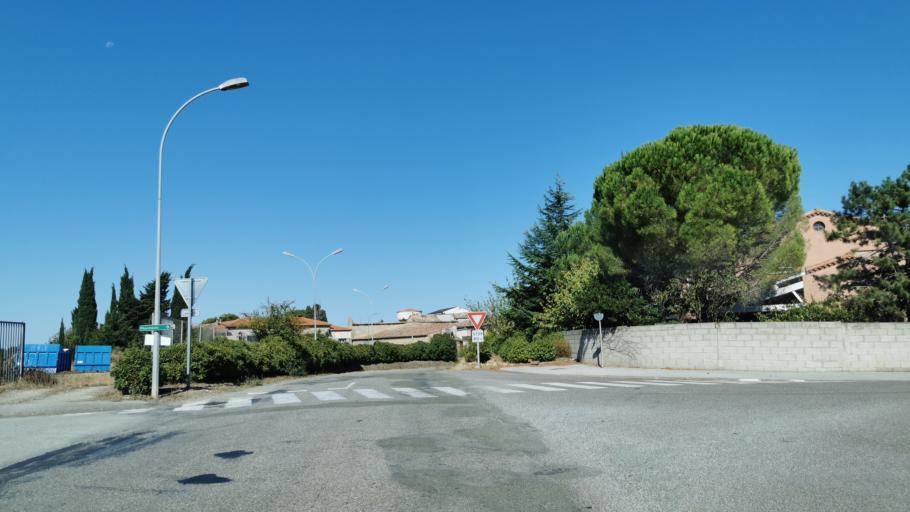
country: FR
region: Languedoc-Roussillon
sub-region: Departement de l'Aude
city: Conques-sur-Orbiel
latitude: 43.2579
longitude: 2.4161
